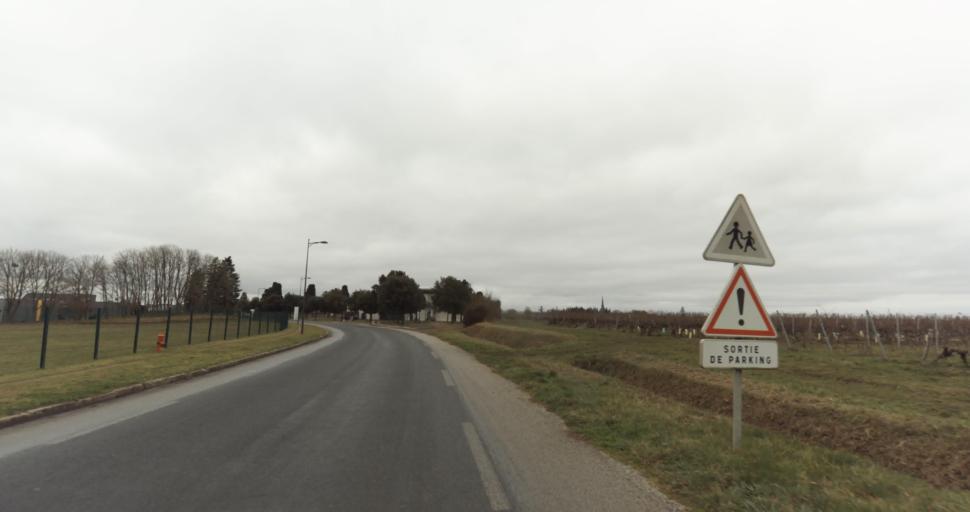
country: FR
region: Pays de la Loire
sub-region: Departement de Maine-et-Loire
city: Montreuil-Bellay
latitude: 47.1313
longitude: -0.1454
